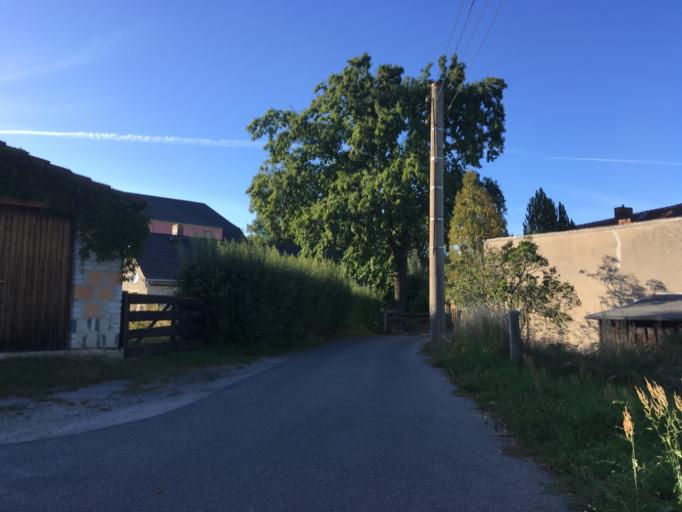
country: DE
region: Saxony
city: Bad Muskau
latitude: 51.5663
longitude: 14.7101
